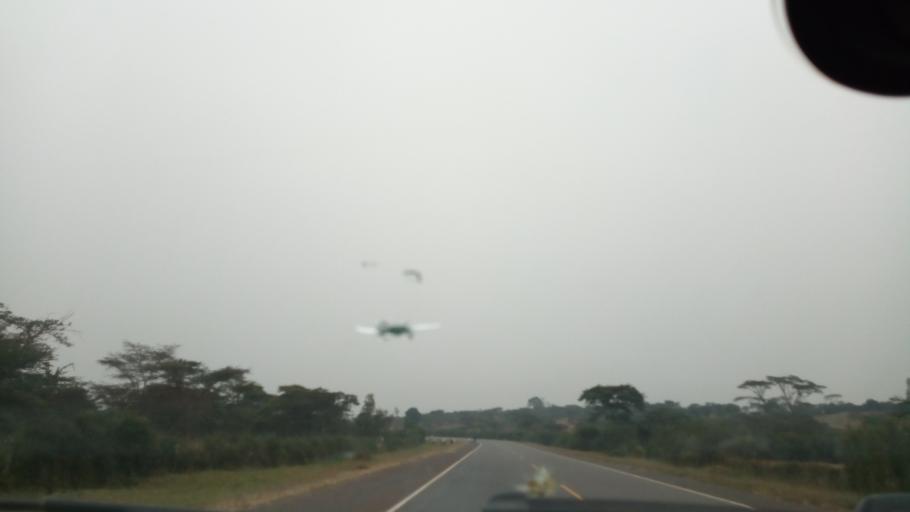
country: UG
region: Western Region
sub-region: Mbarara District
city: Mbarara
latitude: -0.7113
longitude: 30.7139
